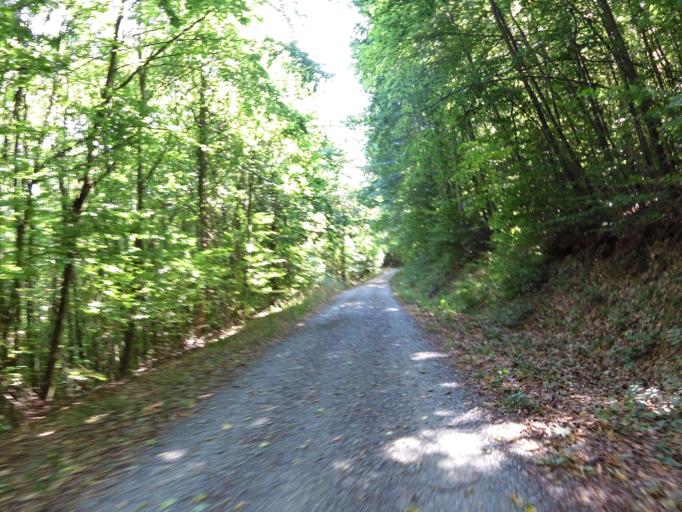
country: DE
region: Bavaria
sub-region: Regierungsbezirk Unterfranken
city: Wuerzburg
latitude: 49.7660
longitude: 9.9082
